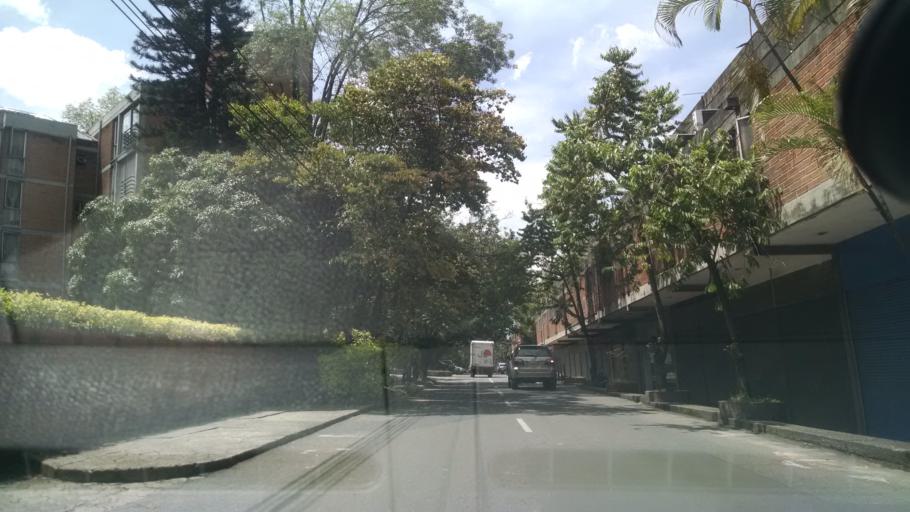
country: CO
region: Antioquia
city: Medellin
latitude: 6.2321
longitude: -75.5686
